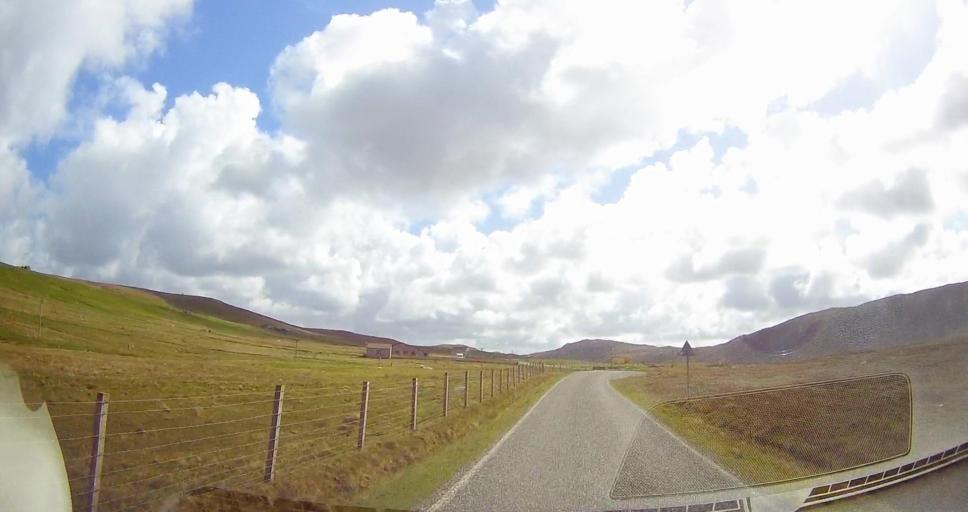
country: GB
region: Scotland
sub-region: Shetland Islands
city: Lerwick
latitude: 60.5735
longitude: -1.3315
